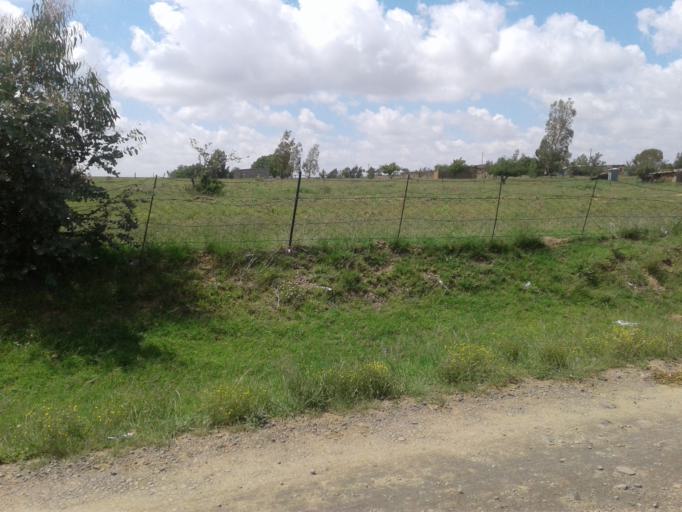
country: LS
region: Mafeteng
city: Mafeteng
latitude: -29.7522
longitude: 27.1131
